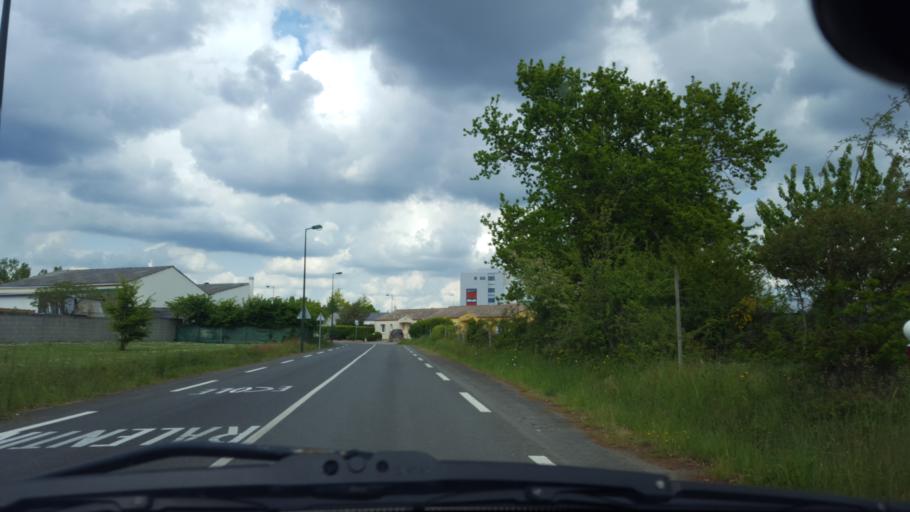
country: FR
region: Pays de la Loire
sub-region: Departement de la Loire-Atlantique
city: Saint-Philbert-de-Grand-Lieu
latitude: 47.0466
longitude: -1.6365
